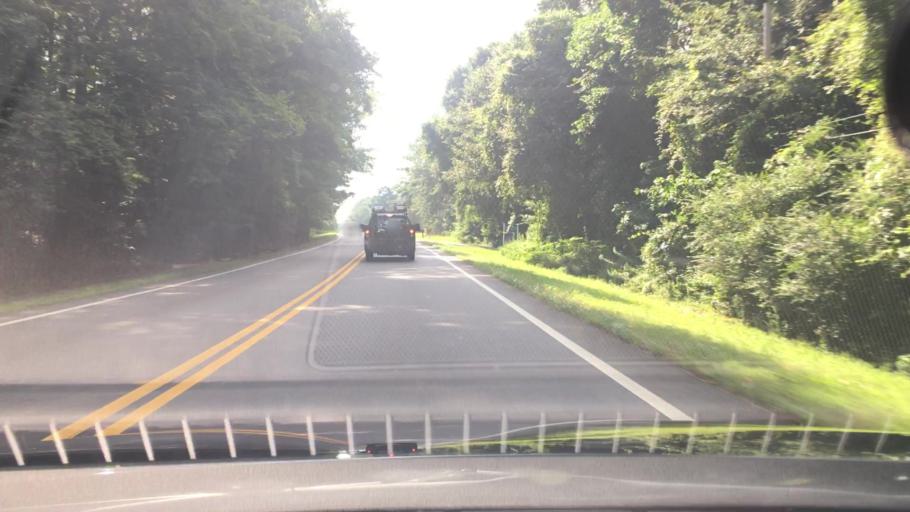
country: US
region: Georgia
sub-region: Coweta County
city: Senoia
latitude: 33.2586
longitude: -84.5024
